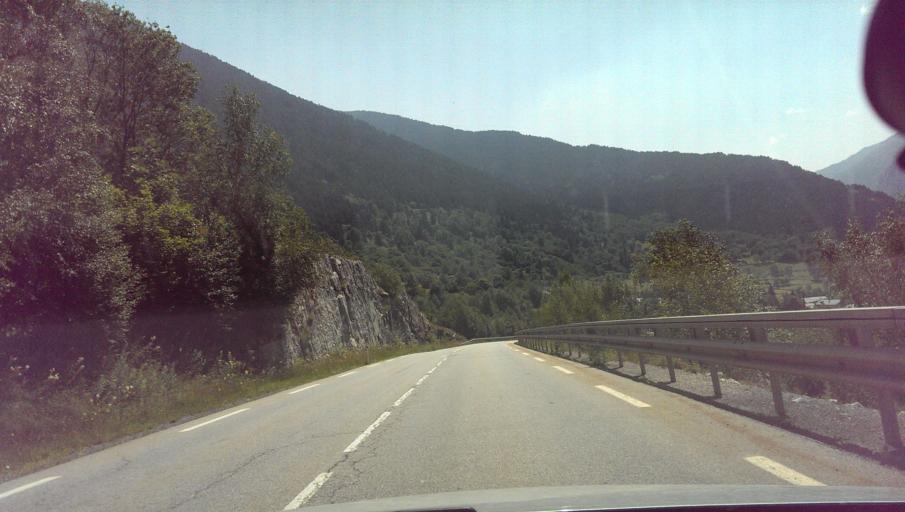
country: AD
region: Encamp
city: Pas de la Casa
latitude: 42.5297
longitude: 1.8233
